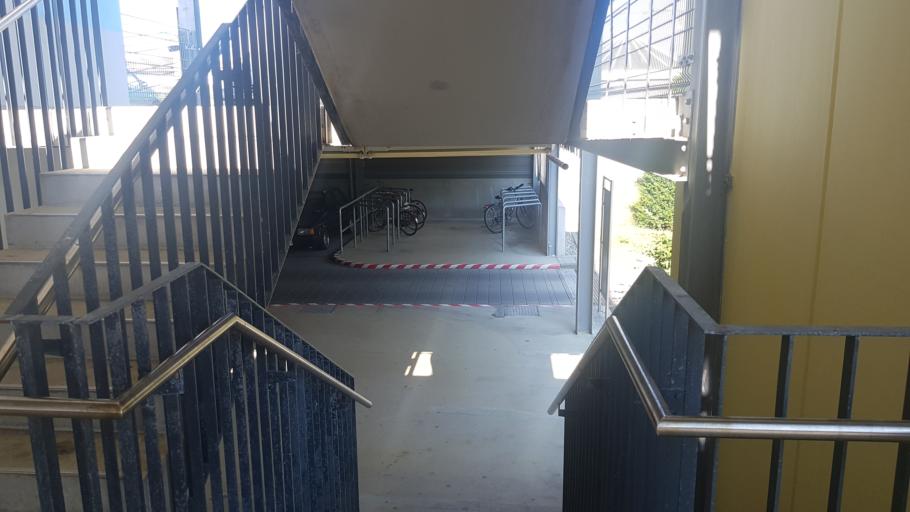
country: DE
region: Baden-Wuerttemberg
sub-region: Regierungsbezirk Stuttgart
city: Bondorf
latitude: 48.5244
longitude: 8.8277
